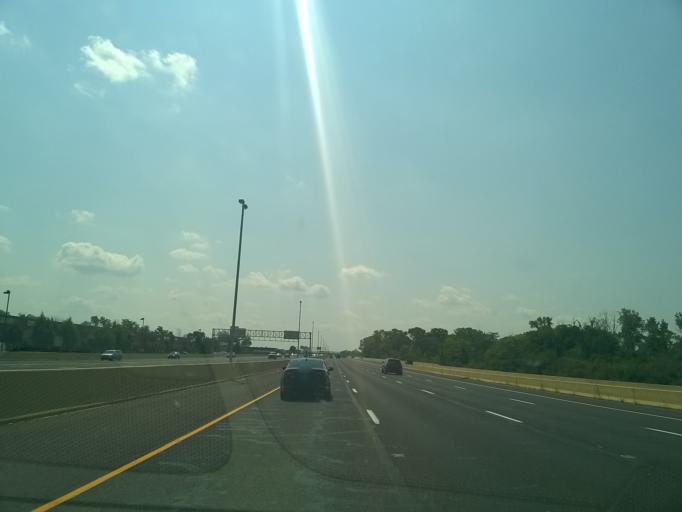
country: US
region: Indiana
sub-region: Boone County
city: Zionsville
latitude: 39.9065
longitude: -86.2700
